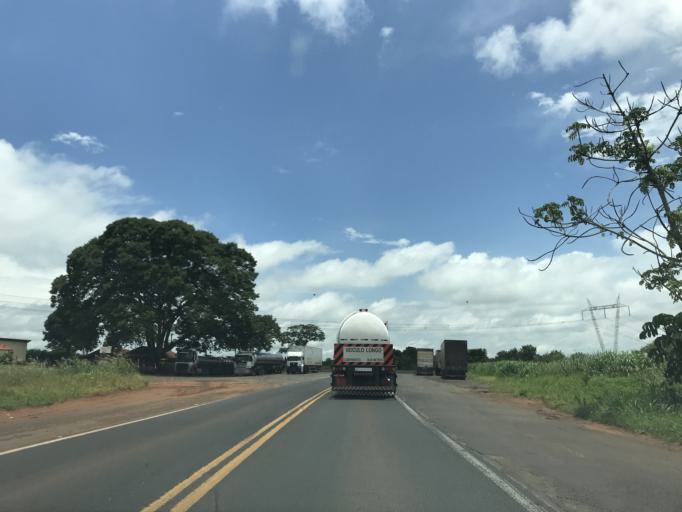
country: BR
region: Minas Gerais
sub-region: Prata
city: Prata
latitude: -19.6296
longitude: -48.9604
